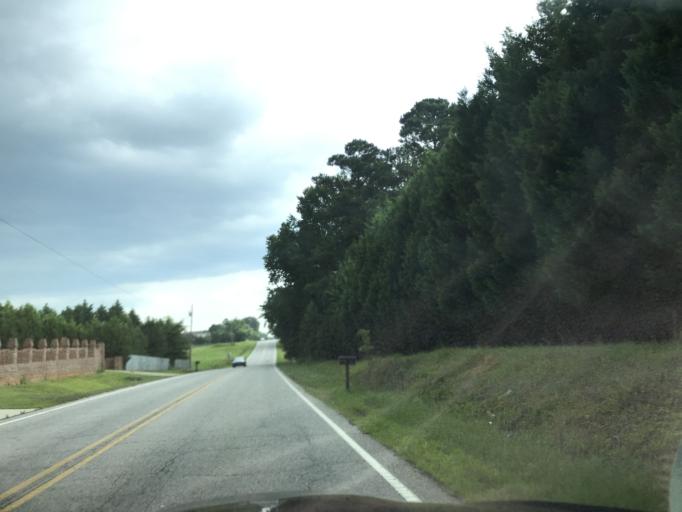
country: US
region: North Carolina
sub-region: Johnston County
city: Four Oaks
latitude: 35.5133
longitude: -78.4864
